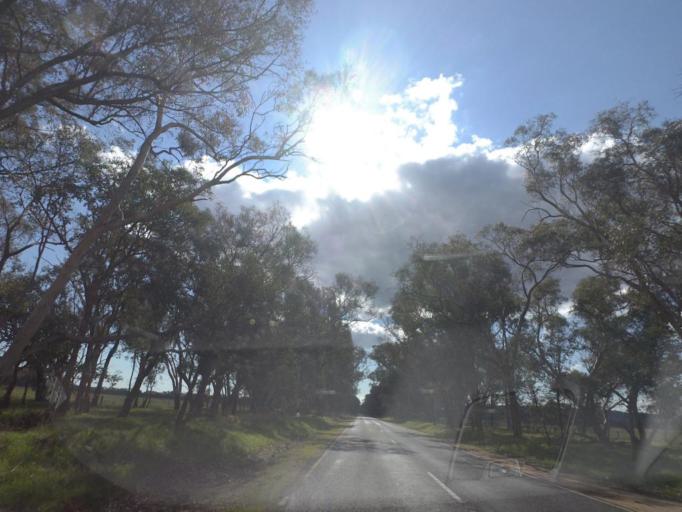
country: AU
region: New South Wales
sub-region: Corowa Shire
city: Howlong
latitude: -36.2119
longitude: 146.6232
